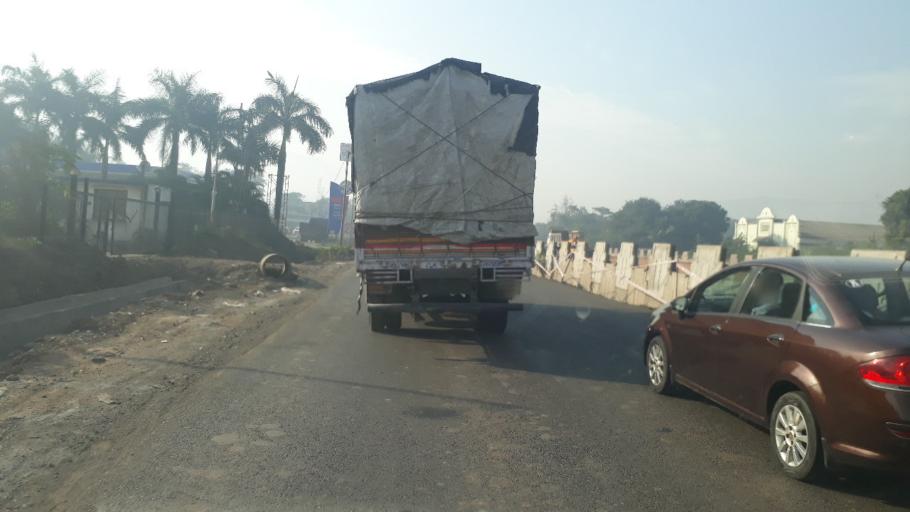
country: IN
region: Maharashtra
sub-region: Raigarh
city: Kalundri
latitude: 18.9299
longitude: 73.1275
